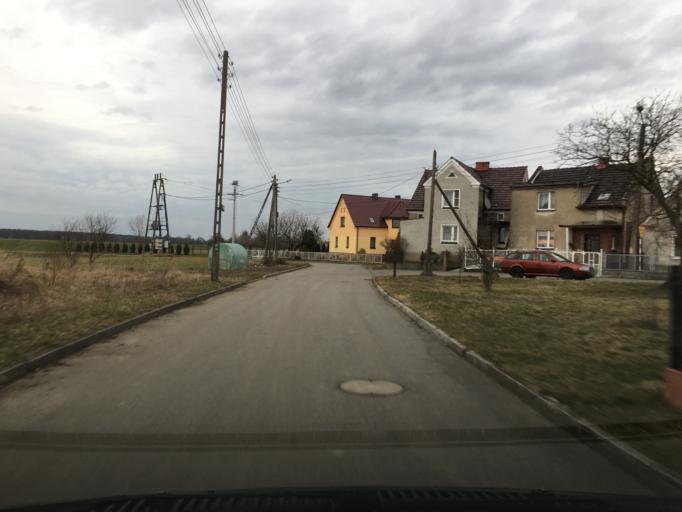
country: PL
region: Opole Voivodeship
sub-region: Powiat kedzierzynsko-kozielski
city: Wiekszyce
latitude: 50.3585
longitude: 18.1181
